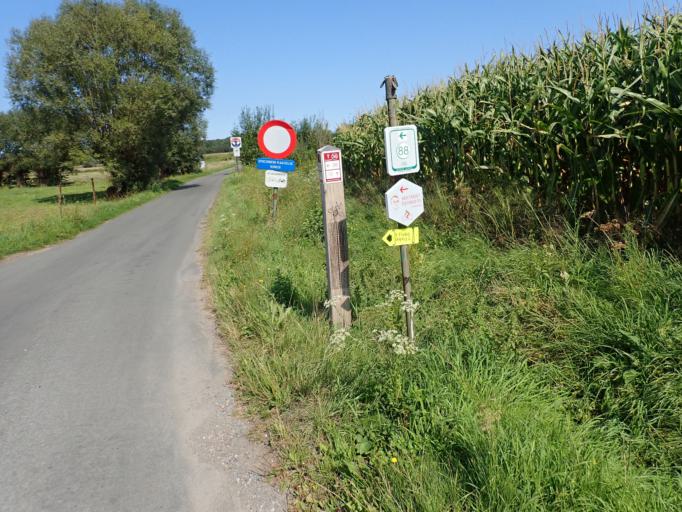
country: BE
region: Flanders
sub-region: Provincie Antwerpen
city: Puurs
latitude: 51.0399
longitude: 4.2884
